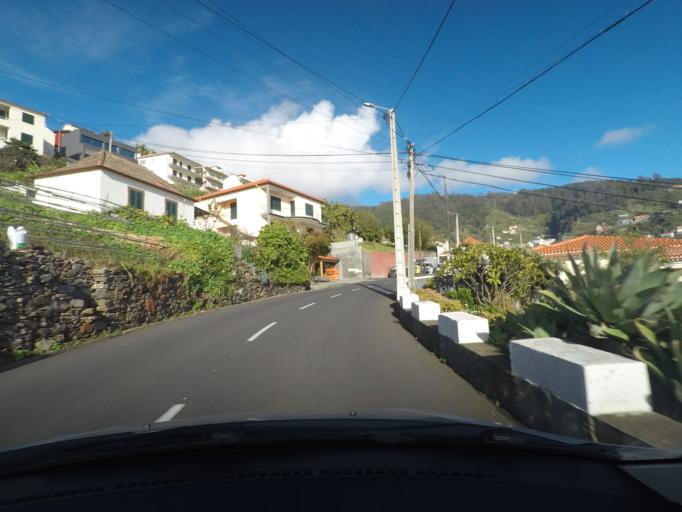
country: PT
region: Madeira
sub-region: Ribeira Brava
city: Campanario
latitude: 32.6696
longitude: -17.0321
